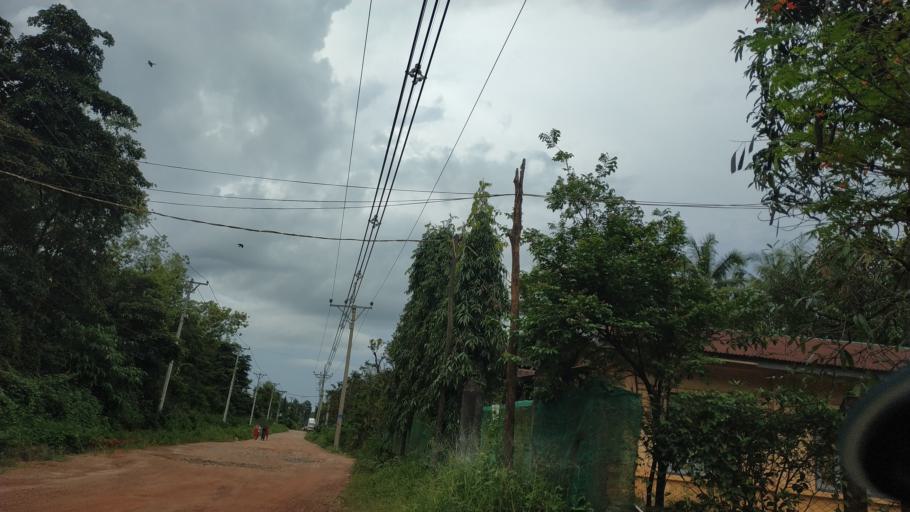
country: MM
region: Tanintharyi
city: Dawei
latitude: 14.0950
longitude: 98.2000
